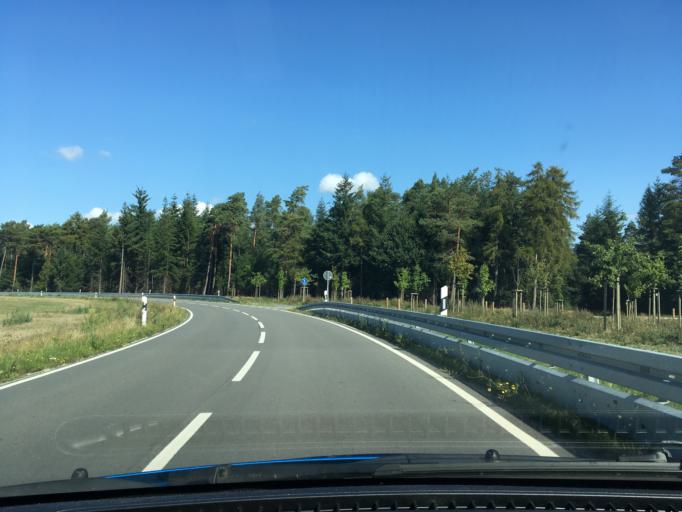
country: DE
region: Lower Saxony
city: Wietzendorf
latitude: 52.8895
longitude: 10.0369
